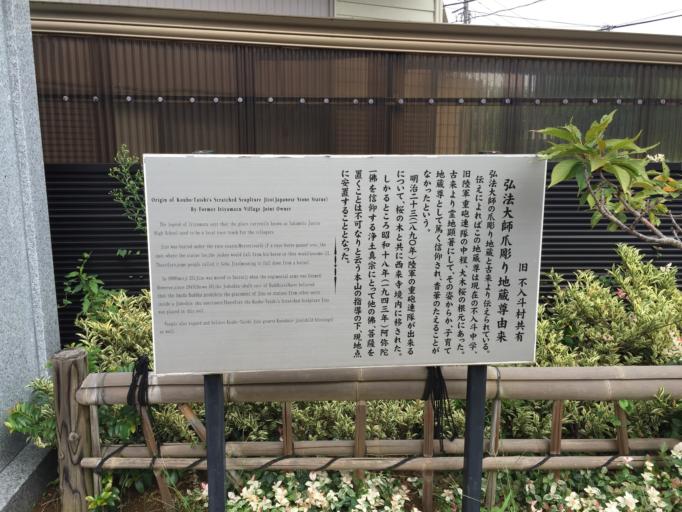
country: JP
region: Kanagawa
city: Yokosuka
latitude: 35.2695
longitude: 139.6617
